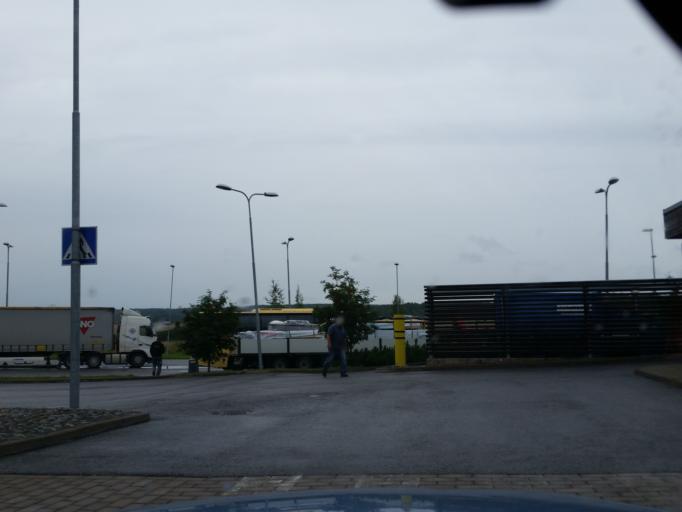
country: FI
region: Varsinais-Suomi
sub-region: Salo
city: Halikko
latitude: 60.4251
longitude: 23.0449
